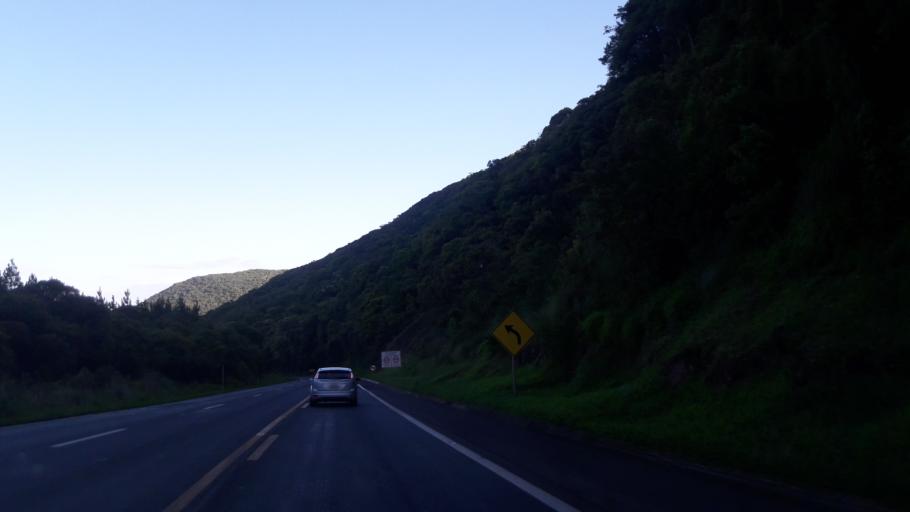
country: BR
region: Parana
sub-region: Prudentopolis
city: Prudentopolis
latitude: -25.3133
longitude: -51.2022
